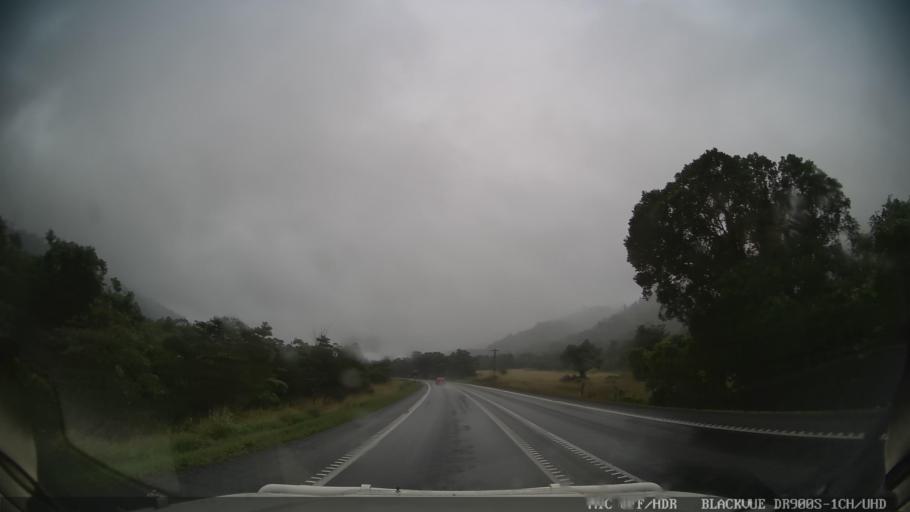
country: AU
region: Queensland
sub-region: Cassowary Coast
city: Innisfail
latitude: -17.8609
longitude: 145.9862
